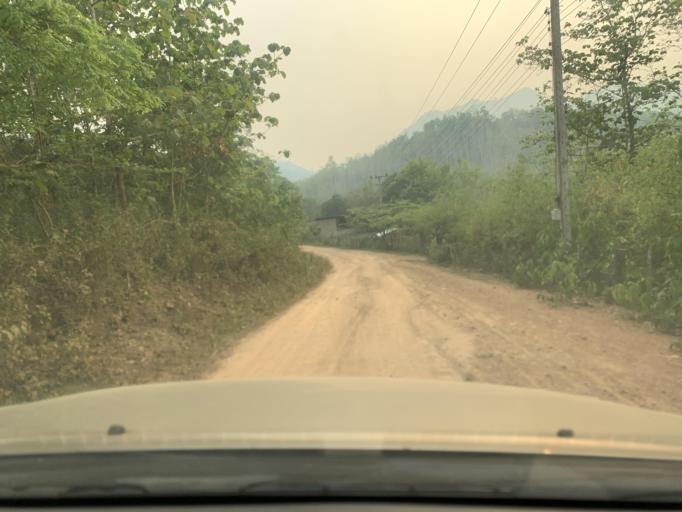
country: LA
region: Louangphabang
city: Louangphabang
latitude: 19.9263
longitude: 102.0755
